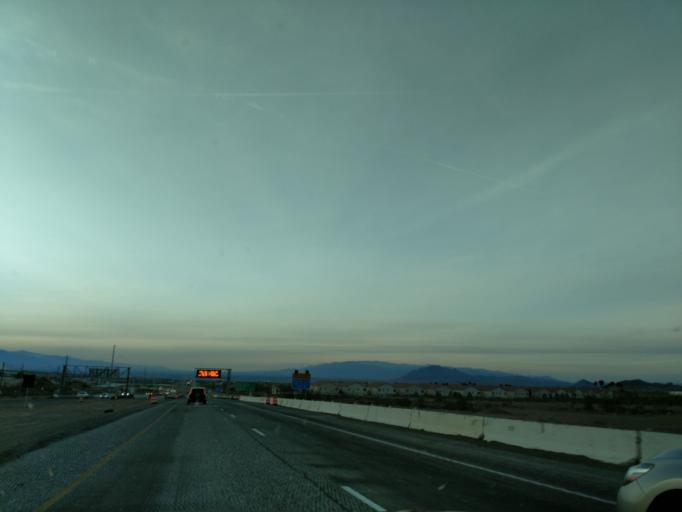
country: US
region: Nevada
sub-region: Clark County
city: Henderson
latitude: 35.9874
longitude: -114.9233
